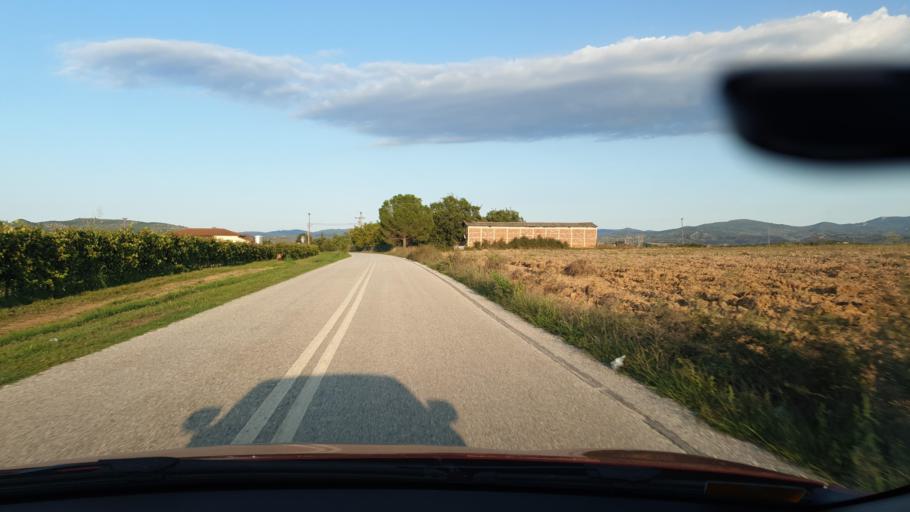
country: GR
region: Central Macedonia
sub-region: Nomos Thessalonikis
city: Nea Apollonia
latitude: 40.5557
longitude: 23.4628
